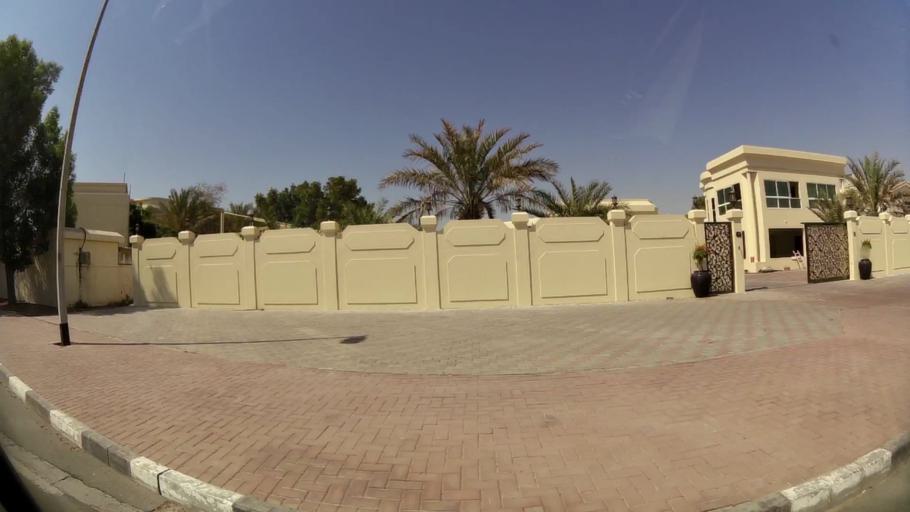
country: AE
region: Ash Shariqah
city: Sharjah
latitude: 25.2677
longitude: 55.3713
